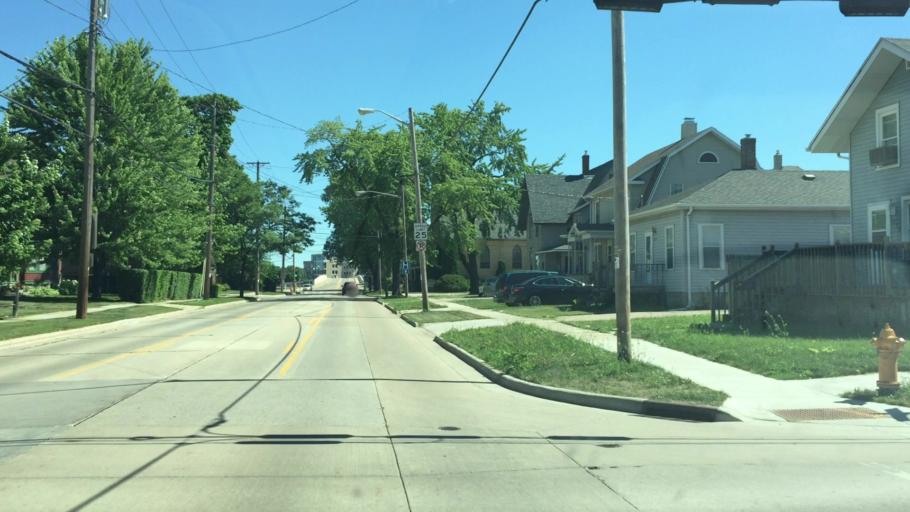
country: US
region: Wisconsin
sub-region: Winnebago County
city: Neenah
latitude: 44.1830
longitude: -88.4587
